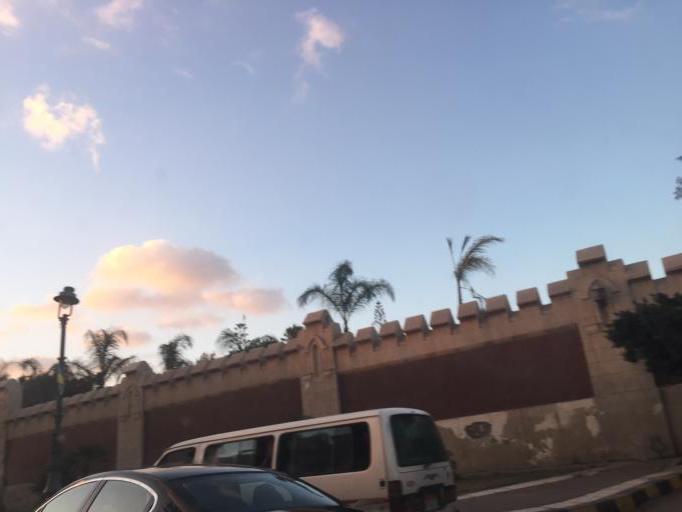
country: EG
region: Alexandria
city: Alexandria
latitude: 31.2808
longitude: 30.0153
